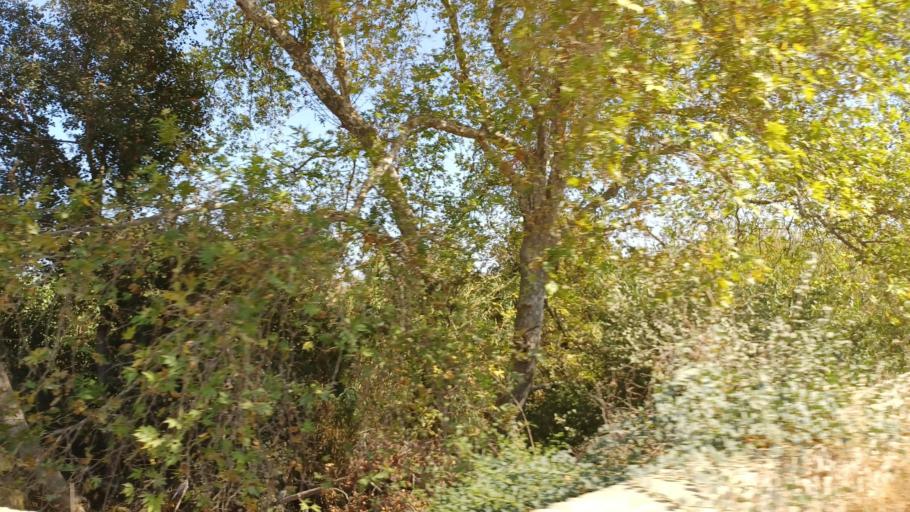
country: CY
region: Pafos
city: Polis
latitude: 35.0030
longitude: 32.4329
